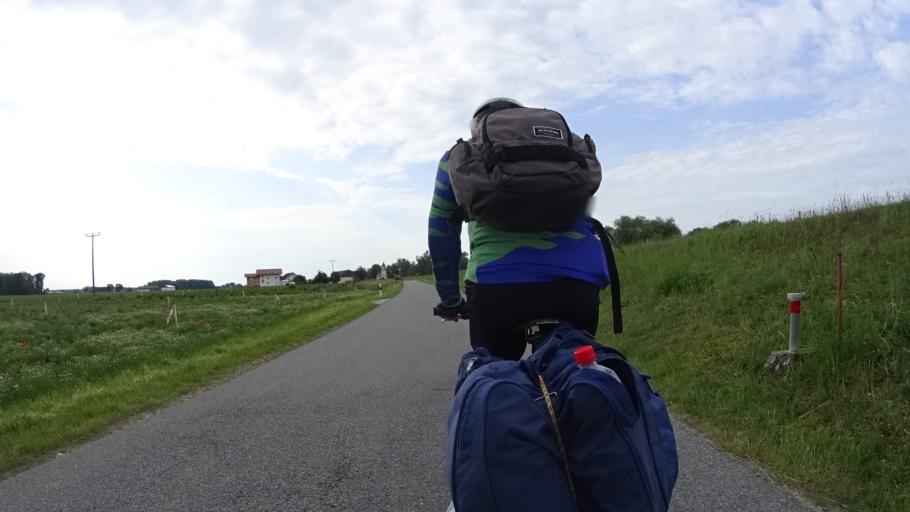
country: DE
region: Bavaria
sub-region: Lower Bavaria
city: Irlbach
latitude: 48.8735
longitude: 12.7548
